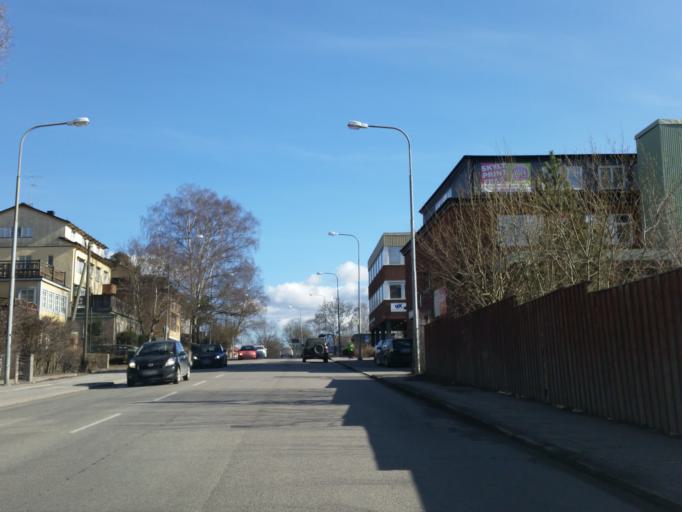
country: SE
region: Stockholm
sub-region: Sundbybergs Kommun
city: Sundbyberg
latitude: 59.3662
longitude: 17.9531
